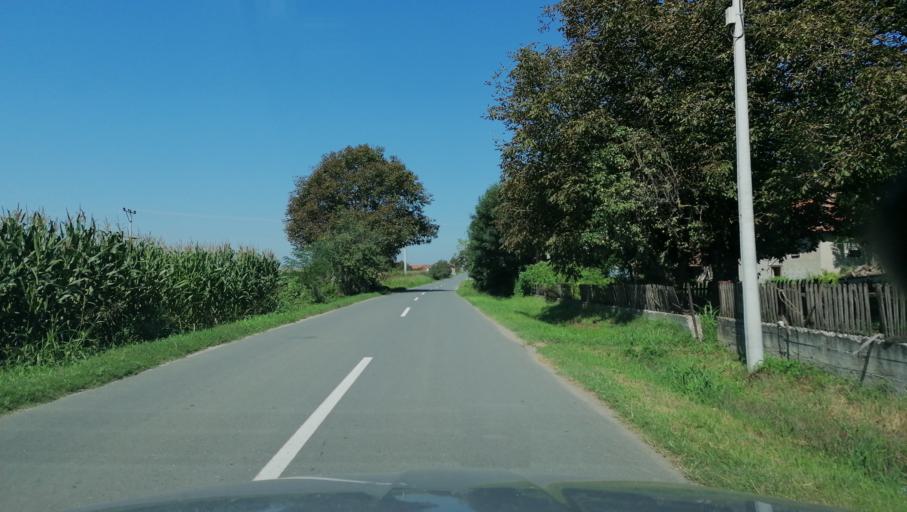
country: RS
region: Central Serbia
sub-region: Raski Okrug
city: Vrnjacka Banja
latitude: 43.6647
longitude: 20.9185
